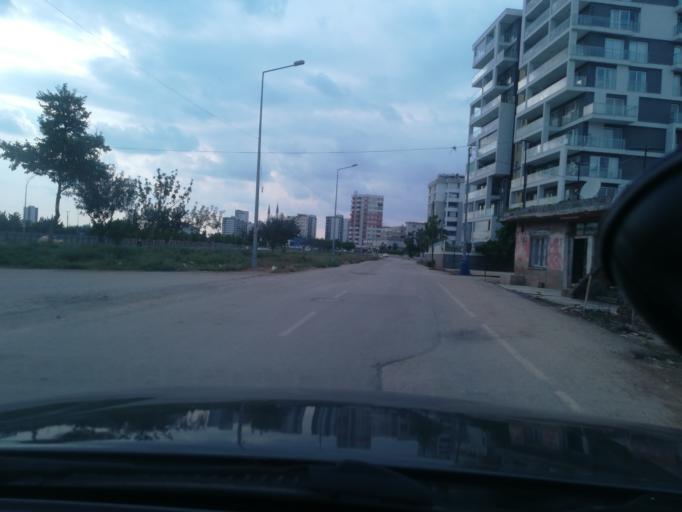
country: TR
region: Adana
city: Seyhan
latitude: 37.0100
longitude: 35.2678
